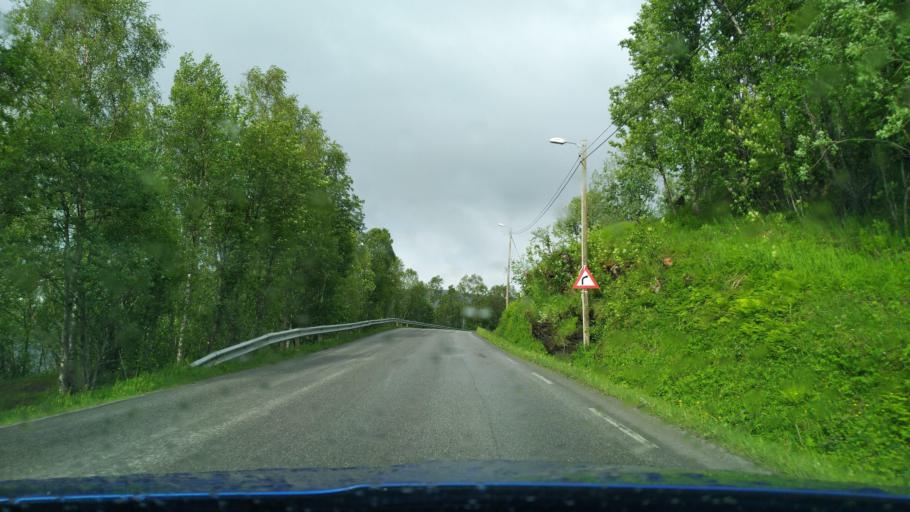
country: NO
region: Troms
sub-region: Sorreisa
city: Sorreisa
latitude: 69.1388
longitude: 18.1002
